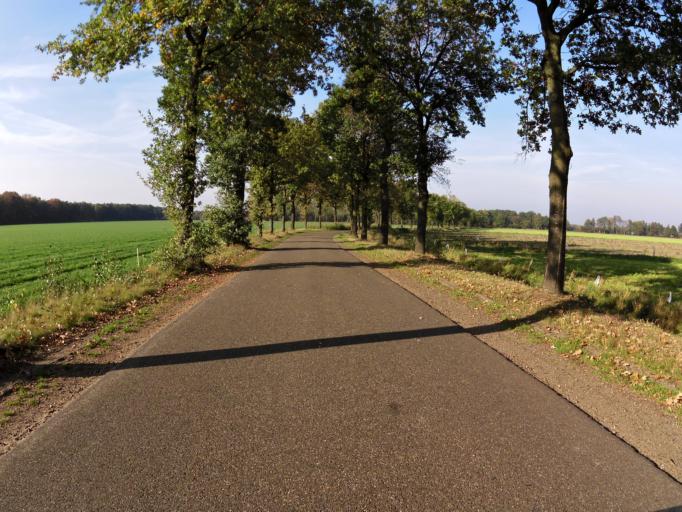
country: NL
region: North Brabant
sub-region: Gemeente Laarbeek
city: Aarle-Rixtel
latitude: 51.5293
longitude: 5.6827
